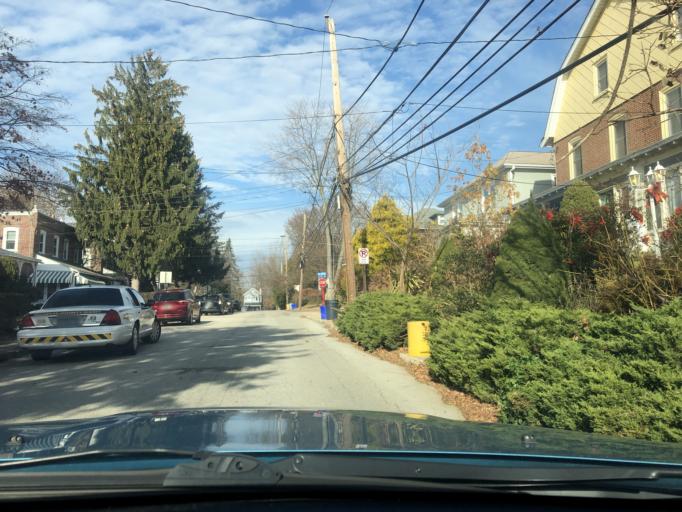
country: US
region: Pennsylvania
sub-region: Delaware County
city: Radnor
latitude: 40.0264
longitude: -75.3386
